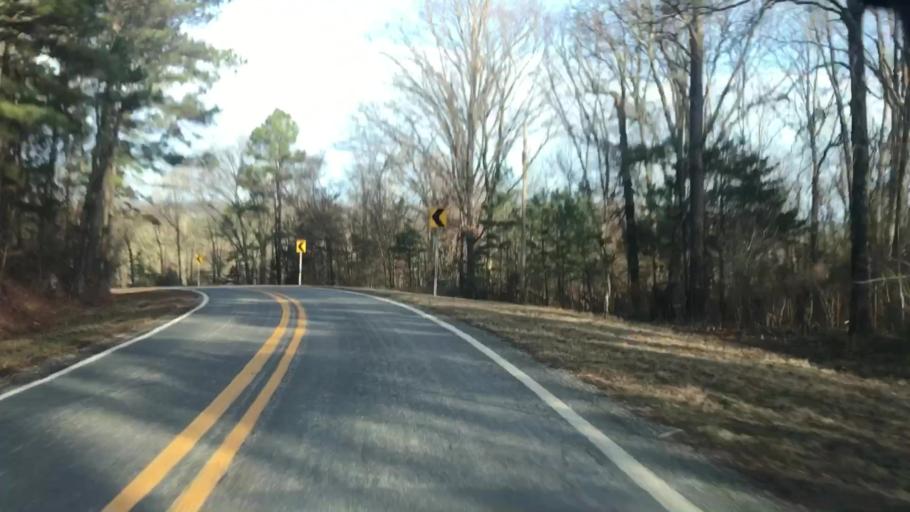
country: US
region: Arkansas
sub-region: Garland County
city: Rockwell
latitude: 34.4871
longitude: -93.2734
